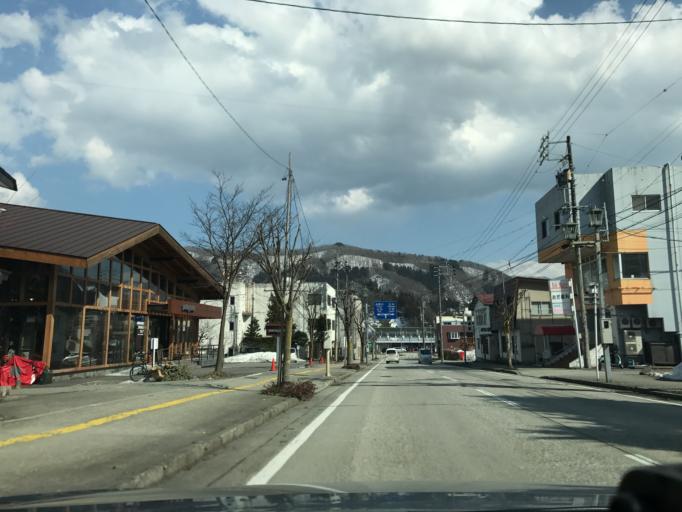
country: JP
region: Nagano
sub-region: Kitaazumi Gun
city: Hakuba
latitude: 36.6964
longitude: 137.8614
